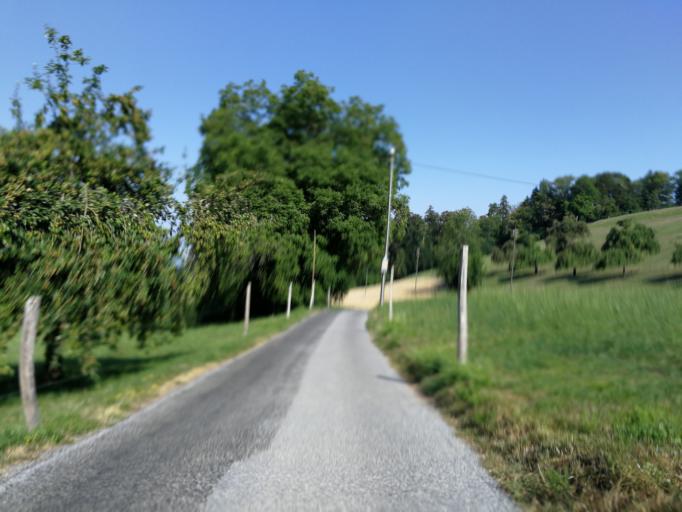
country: CH
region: Zurich
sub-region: Bezirk Meilen
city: Herrliberg
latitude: 47.3006
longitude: 8.6209
